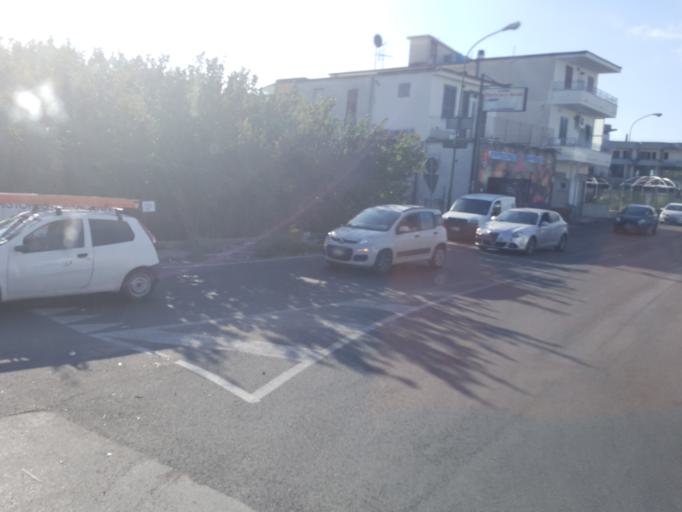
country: IT
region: Campania
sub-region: Provincia di Napoli
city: Nola
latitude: 40.9166
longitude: 14.5260
